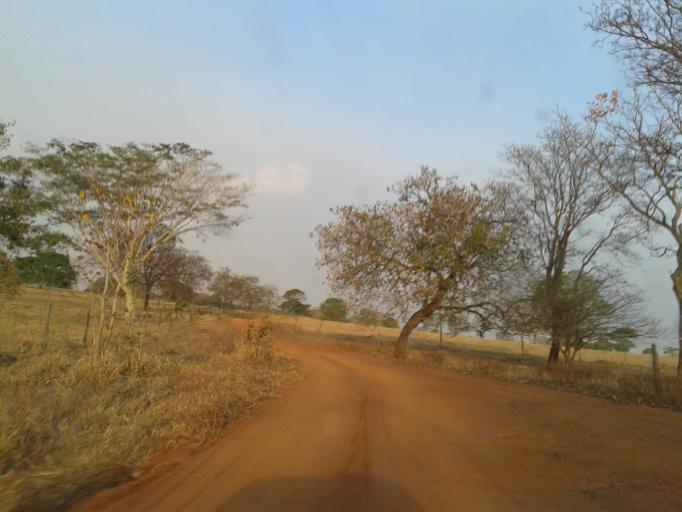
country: BR
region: Minas Gerais
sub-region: Capinopolis
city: Capinopolis
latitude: -18.8056
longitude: -49.7522
